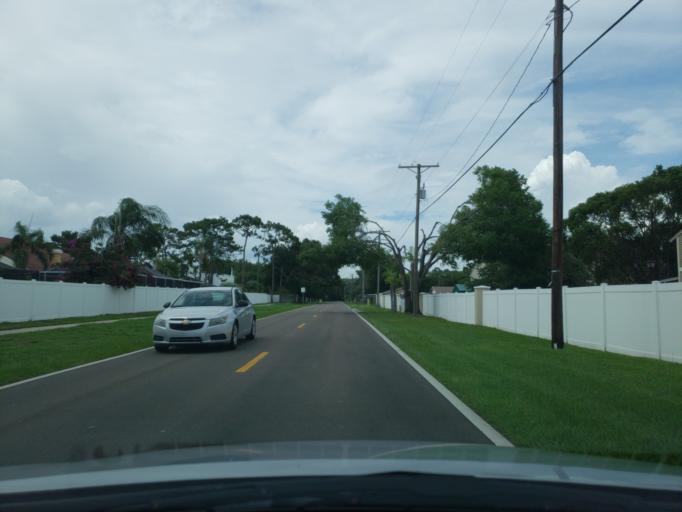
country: US
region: Florida
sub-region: Hillsborough County
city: Town 'n' Country
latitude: 28.0322
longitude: -82.5581
